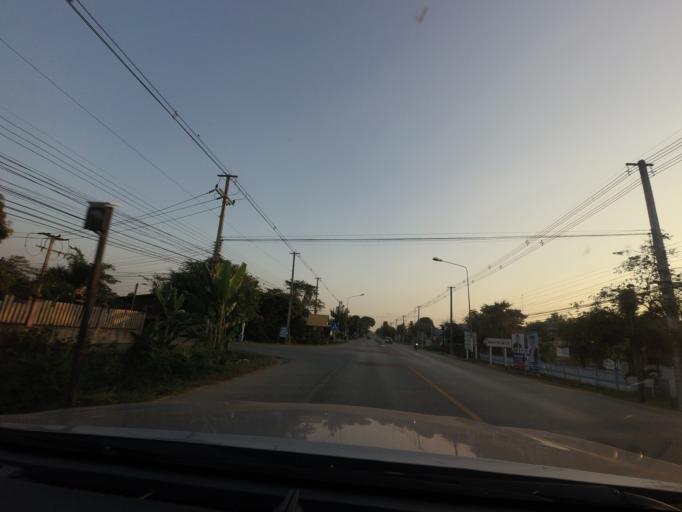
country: TH
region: Sukhothai
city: Si Samrong
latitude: 17.1209
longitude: 99.8509
